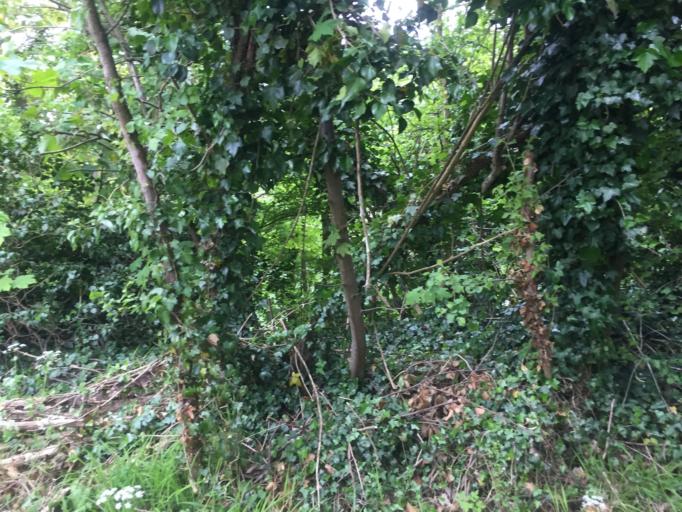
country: GB
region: England
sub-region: Royal Borough of Windsor and Maidenhead
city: Bray
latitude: 51.5065
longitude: -0.6849
